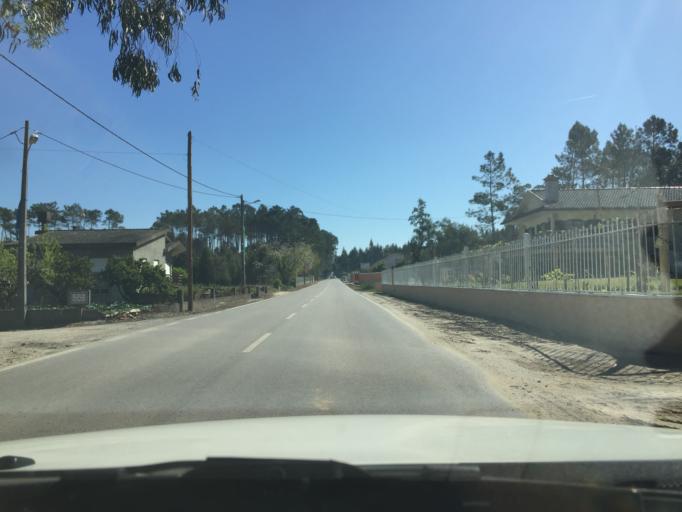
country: PT
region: Coimbra
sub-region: Cantanhede
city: Cantanhede
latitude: 40.4186
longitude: -8.5571
